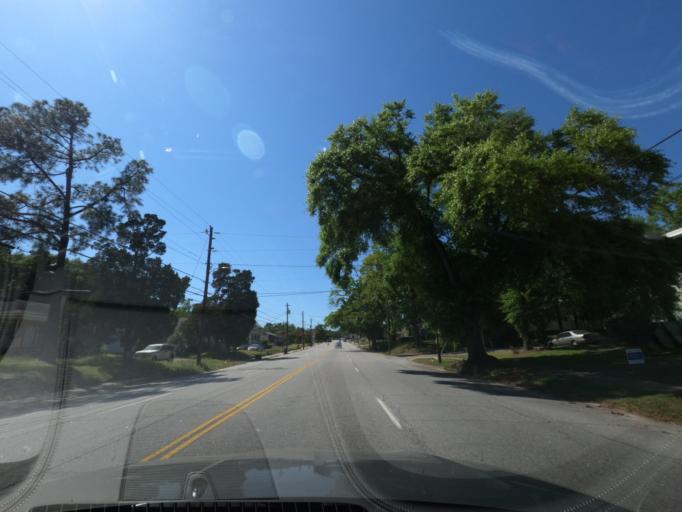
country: US
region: Georgia
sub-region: Richmond County
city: Augusta
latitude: 33.4687
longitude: -82.0074
